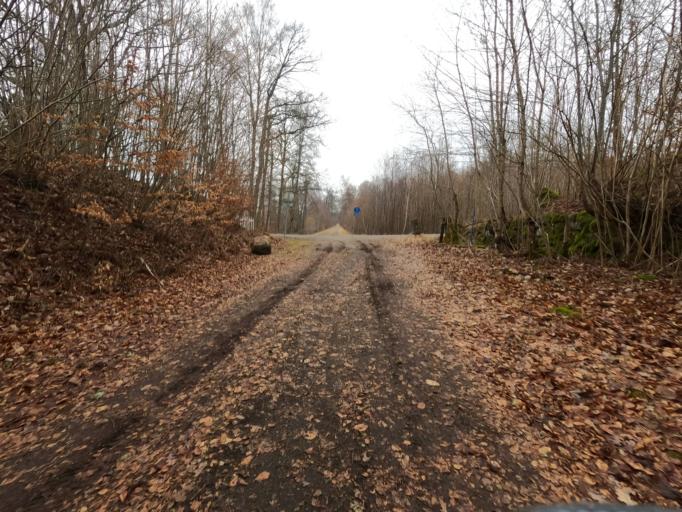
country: SE
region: Kronoberg
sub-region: Markaryds Kommun
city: Stromsnasbruk
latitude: 56.8051
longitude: 13.6826
